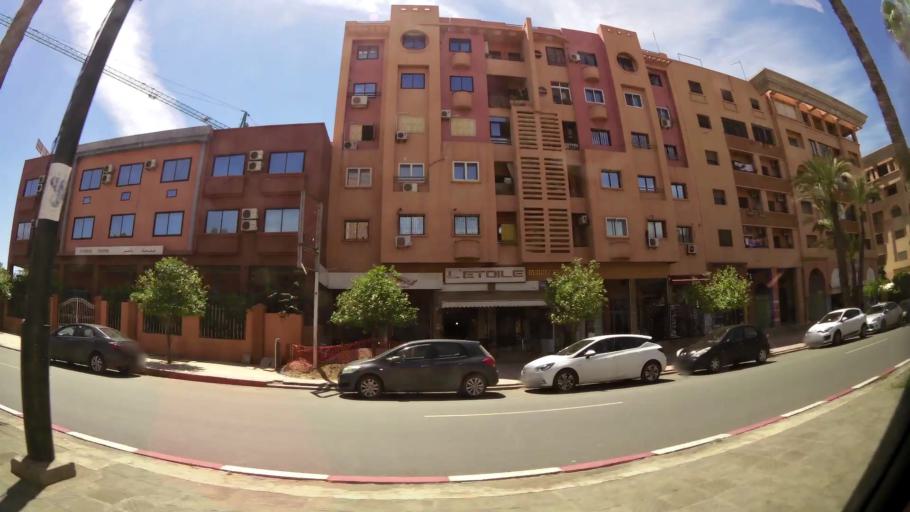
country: MA
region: Marrakech-Tensift-Al Haouz
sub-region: Marrakech
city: Marrakesh
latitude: 31.6570
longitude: -8.0045
